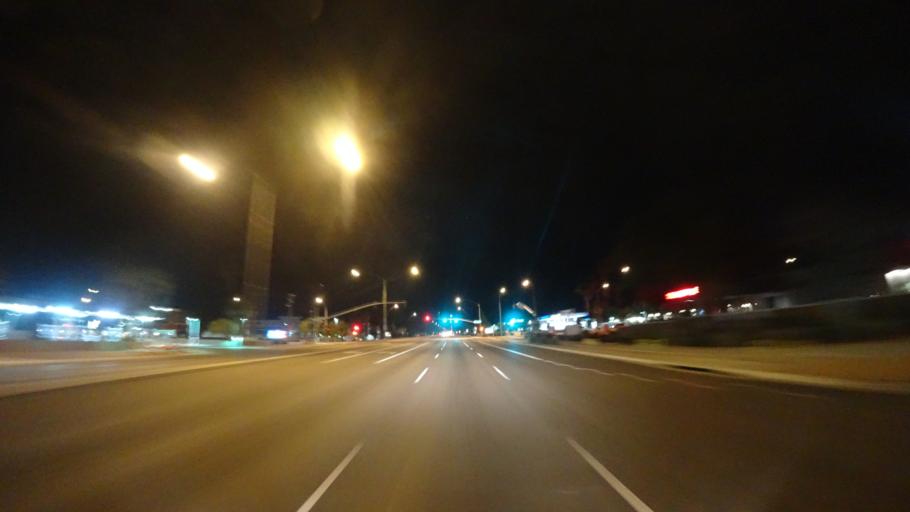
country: US
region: Arizona
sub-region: Maricopa County
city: Gilbert
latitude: 33.3930
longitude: -111.7192
